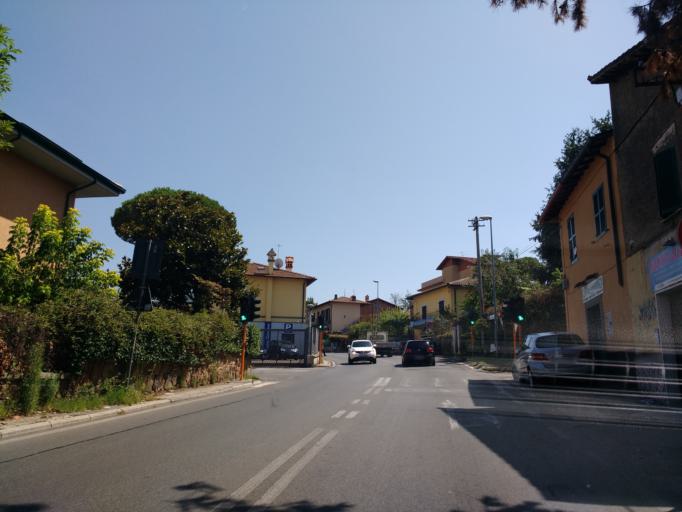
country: IT
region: Latium
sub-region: Citta metropolitana di Roma Capitale
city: Grottaferrata
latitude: 41.7805
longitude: 12.6847
